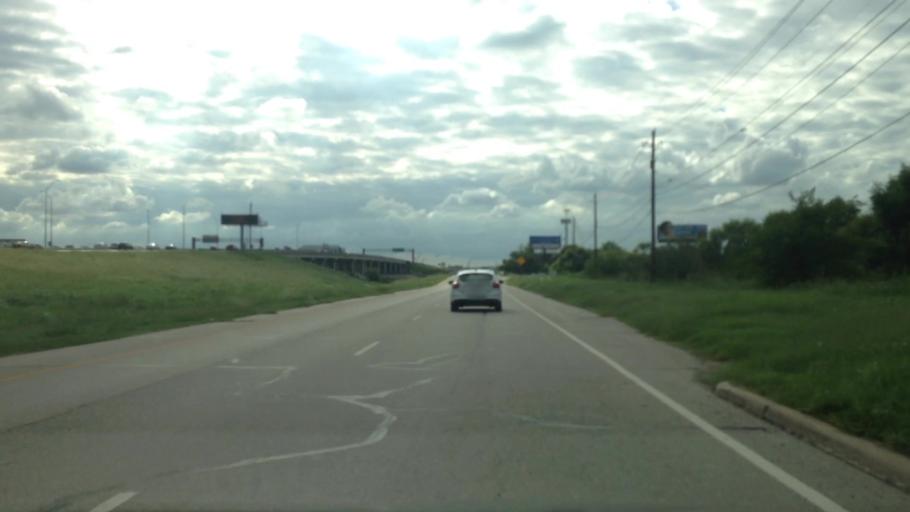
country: US
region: Texas
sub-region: Dallas County
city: Farmers Branch
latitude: 32.9087
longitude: -96.9037
